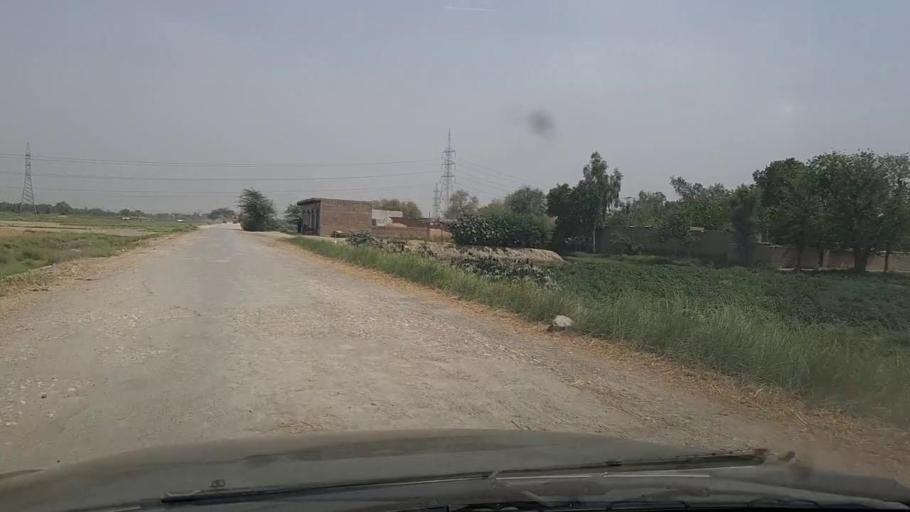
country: PK
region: Sindh
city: Shikarpur
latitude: 27.9243
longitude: 68.6696
